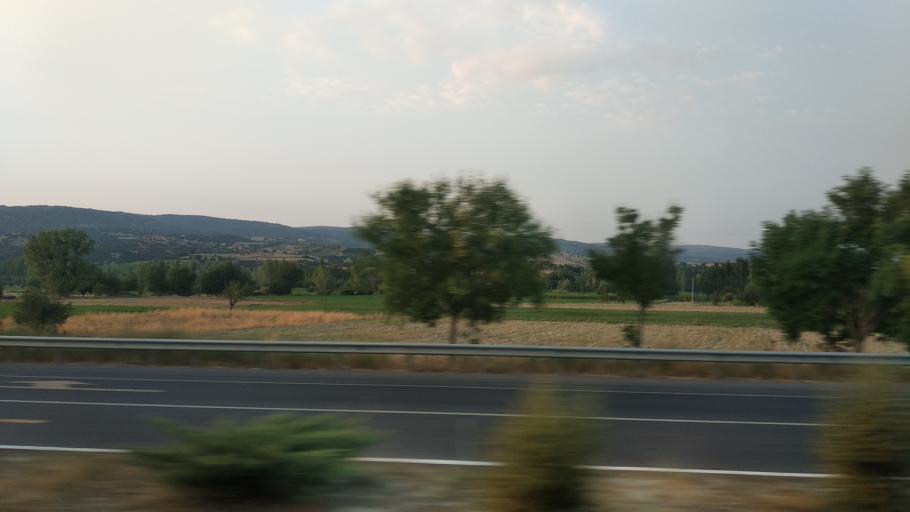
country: TR
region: Manisa
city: Selendi
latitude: 38.6213
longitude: 28.9183
